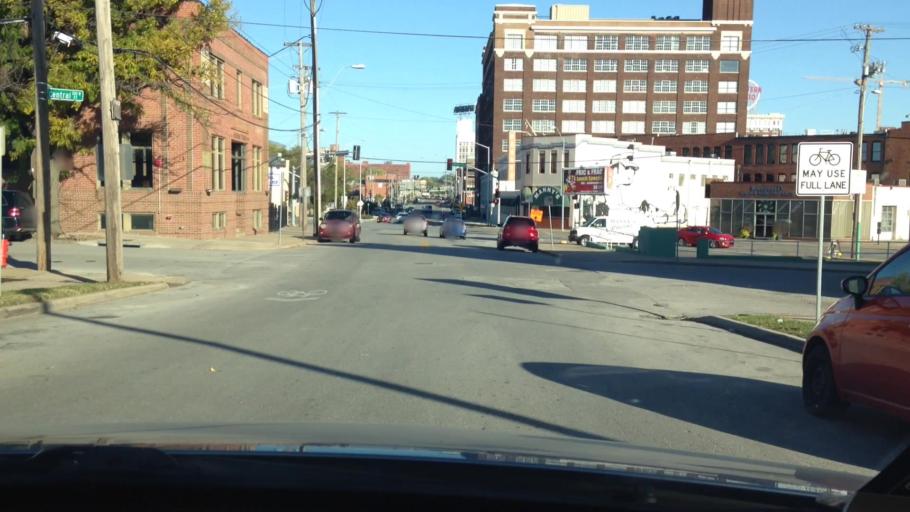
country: US
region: Missouri
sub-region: Jackson County
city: Kansas City
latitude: 39.0892
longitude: -94.5879
